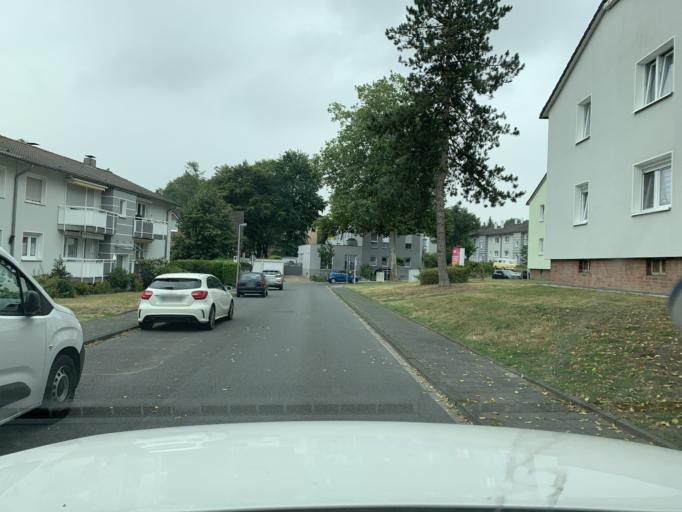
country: DE
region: North Rhine-Westphalia
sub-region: Regierungsbezirk Dusseldorf
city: Muelheim (Ruhr)
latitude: 51.4013
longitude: 6.8734
